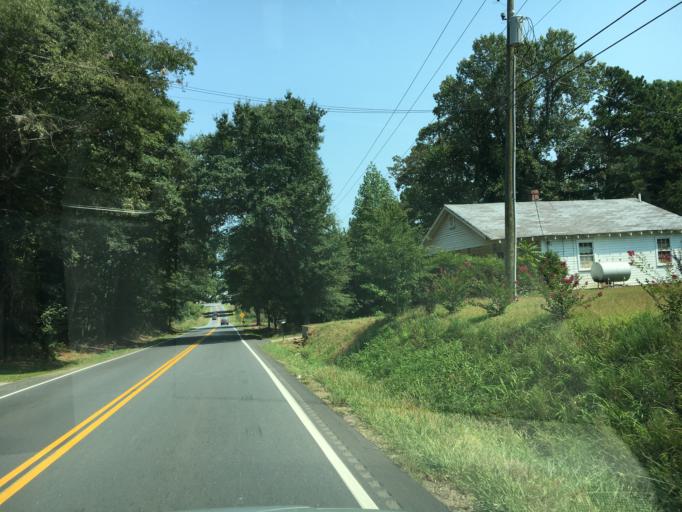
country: US
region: South Carolina
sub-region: Spartanburg County
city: Valley Falls
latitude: 35.0100
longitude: -81.9509
